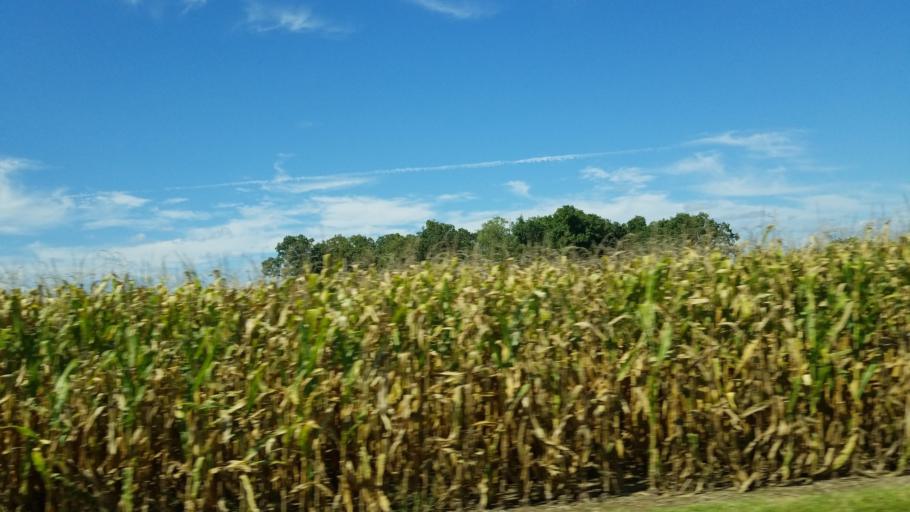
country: US
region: Illinois
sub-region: Williamson County
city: Johnston City
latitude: 37.7904
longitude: -88.7684
